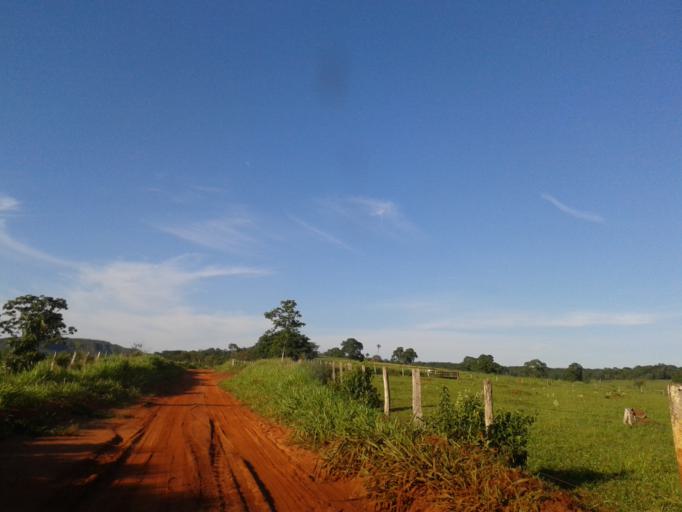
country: BR
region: Minas Gerais
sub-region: Santa Vitoria
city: Santa Vitoria
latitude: -18.9633
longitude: -49.8719
